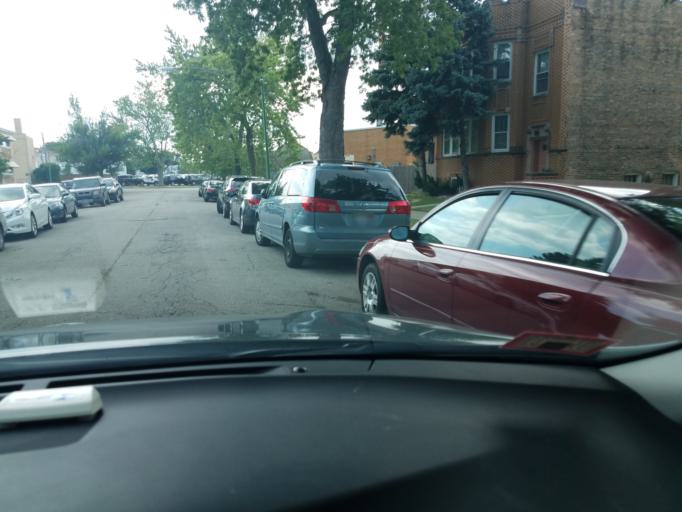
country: US
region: Illinois
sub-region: Cook County
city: Harwood Heights
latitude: 41.9818
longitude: -87.7720
